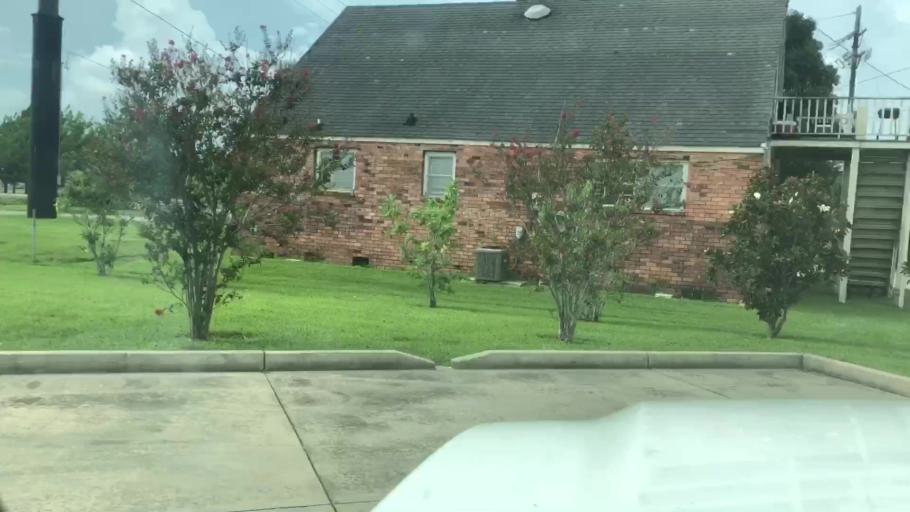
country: US
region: Louisiana
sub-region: Iberia Parish
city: New Iberia
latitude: 29.9835
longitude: -91.8561
